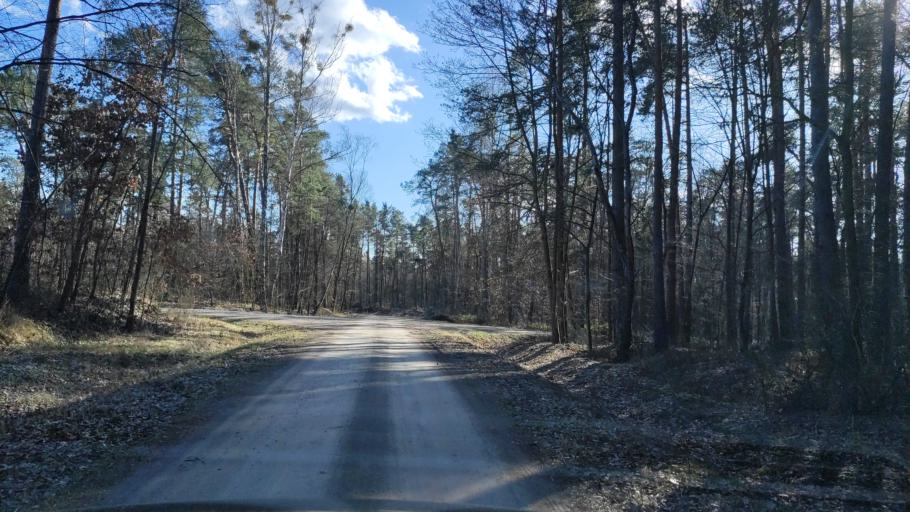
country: PL
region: Masovian Voivodeship
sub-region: Powiat radomski
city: Jedlnia-Letnisko
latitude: 51.4437
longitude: 21.2931
